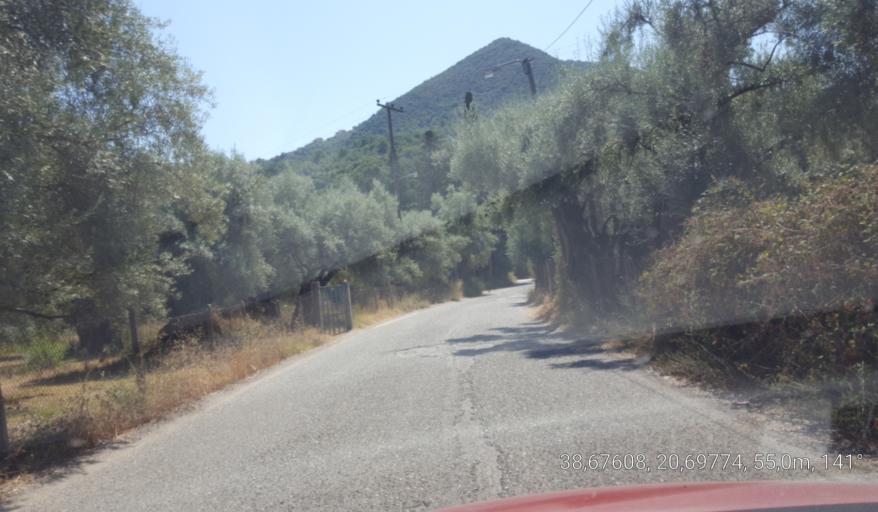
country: GR
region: Ionian Islands
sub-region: Lefkada
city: Nidri
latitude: 38.6761
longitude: 20.6978
